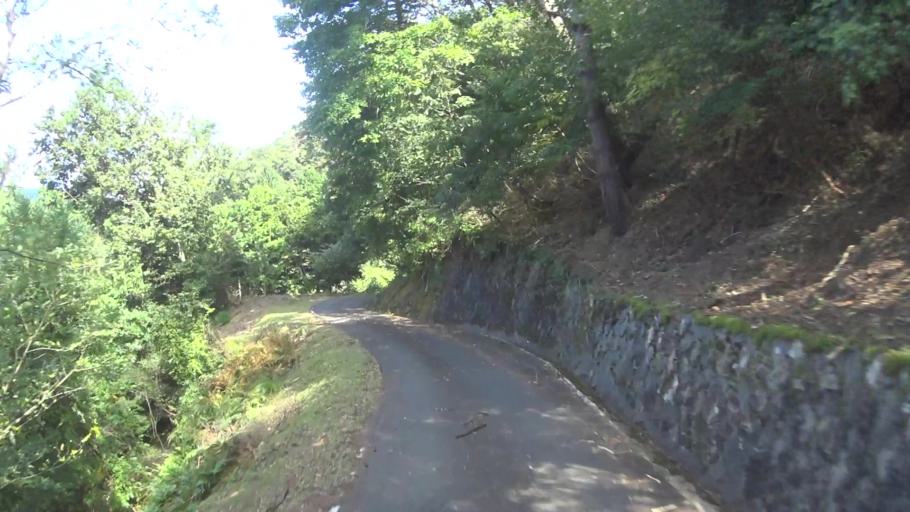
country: JP
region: Hyogo
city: Toyooka
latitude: 35.6066
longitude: 134.9944
